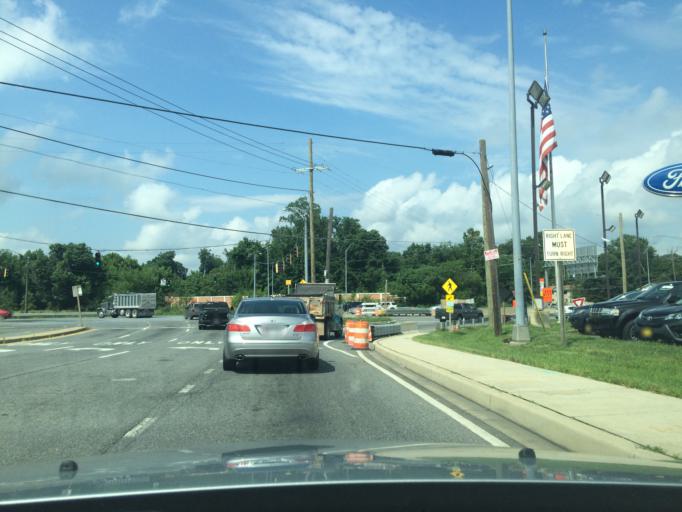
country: US
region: Maryland
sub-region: Prince George's County
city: Camp Springs
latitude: 38.8219
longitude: -76.9204
